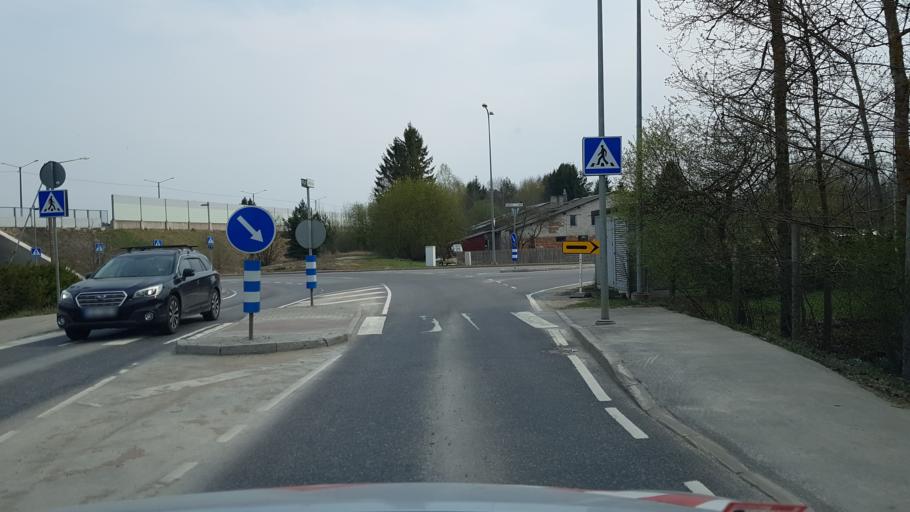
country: EE
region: Harju
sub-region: Rae vald
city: Jueri
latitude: 59.3783
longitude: 24.8420
